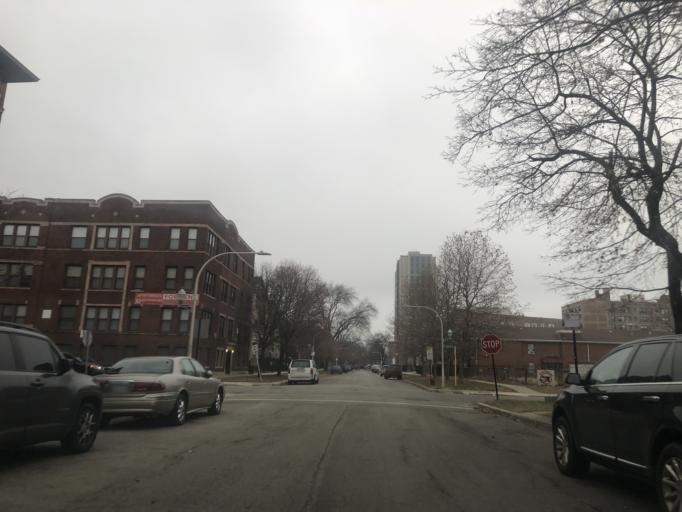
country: US
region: Illinois
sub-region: Cook County
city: Chicago
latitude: 41.7820
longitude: -87.5978
